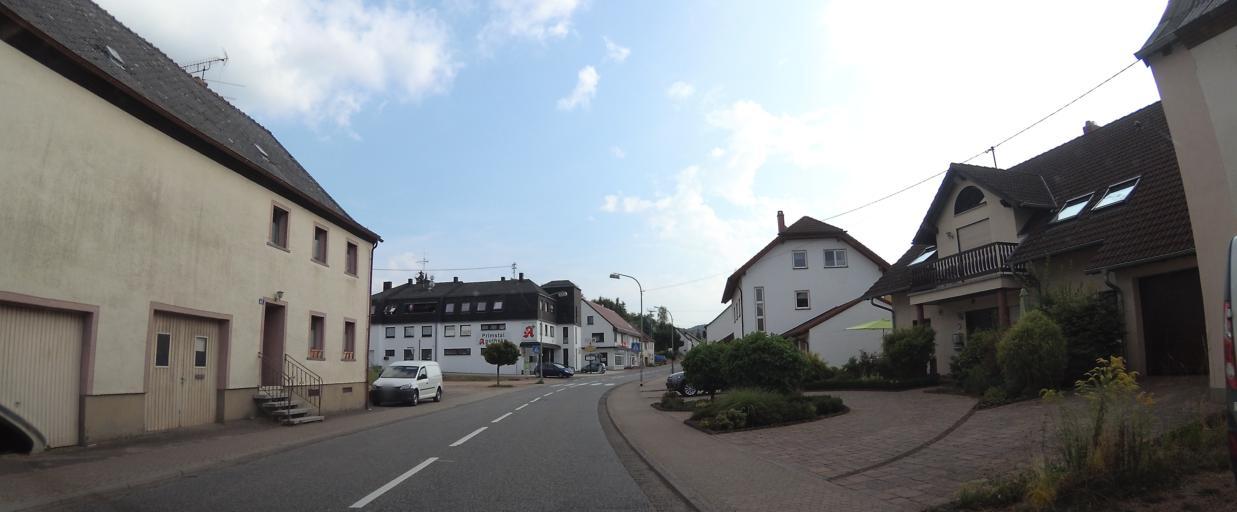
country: DE
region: Saarland
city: Tholey
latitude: 49.5348
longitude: 6.9760
